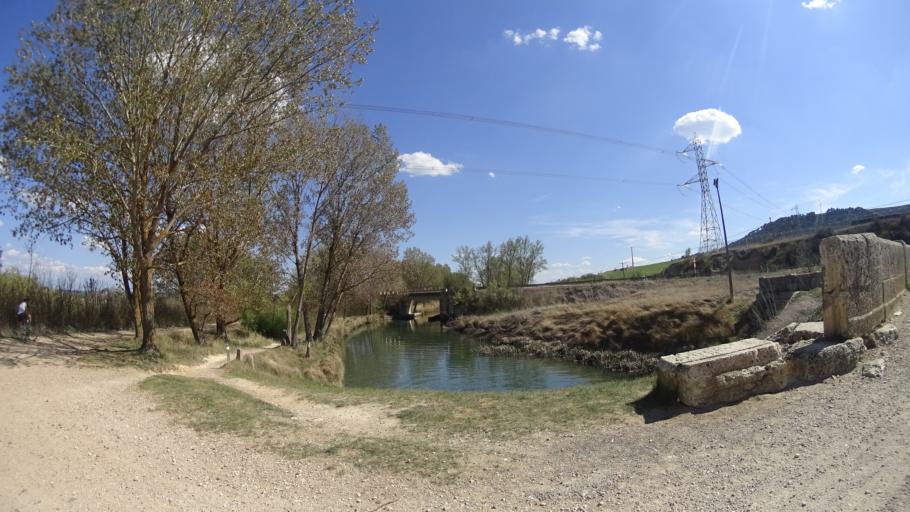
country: ES
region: Castille and Leon
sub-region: Provincia de Palencia
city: Grijota
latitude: 42.0298
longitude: -4.5816
